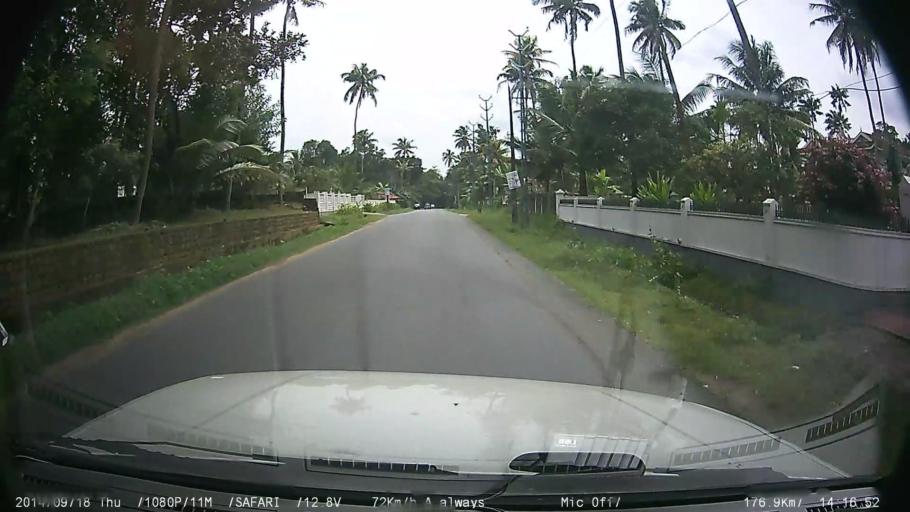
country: IN
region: Kerala
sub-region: Ernakulam
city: Kotamangalam
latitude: 10.0835
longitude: 76.6339
